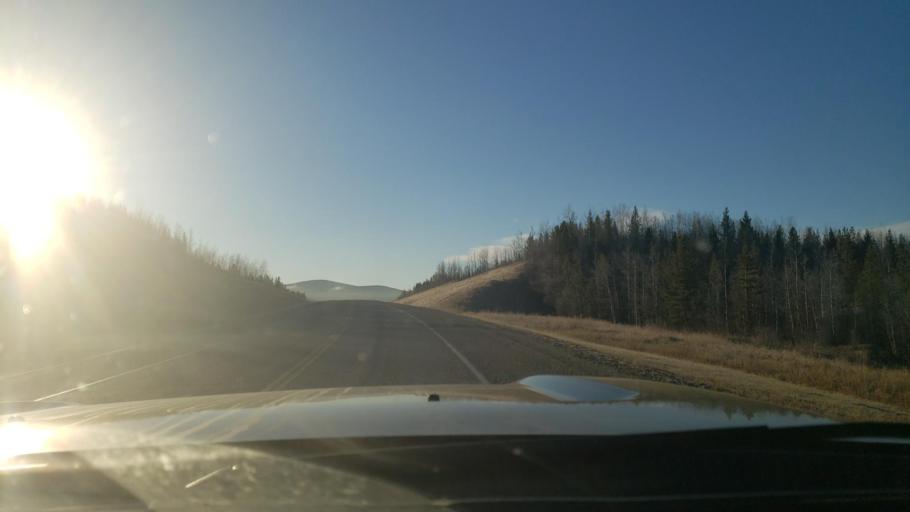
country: CA
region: Yukon
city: Watson Lake
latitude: 59.8149
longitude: -127.4860
